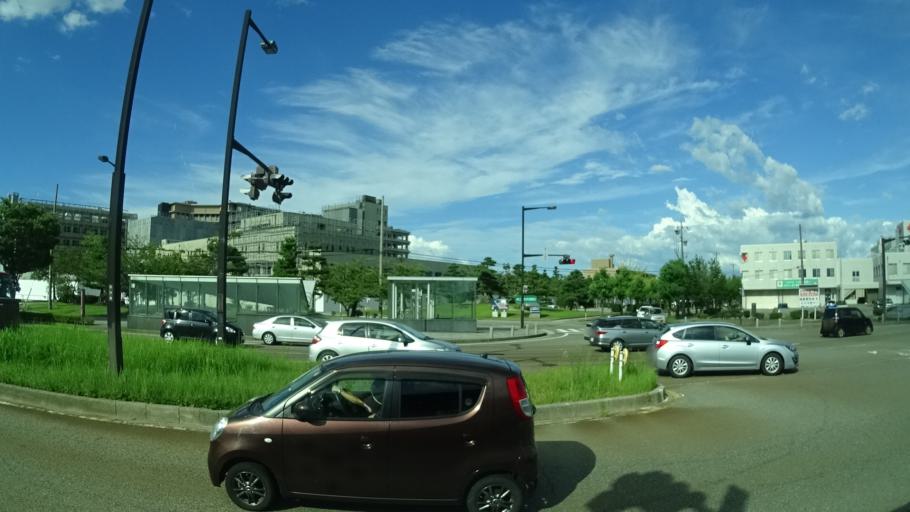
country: JP
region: Ishikawa
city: Kanazawa-shi
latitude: 36.5941
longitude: 136.6280
